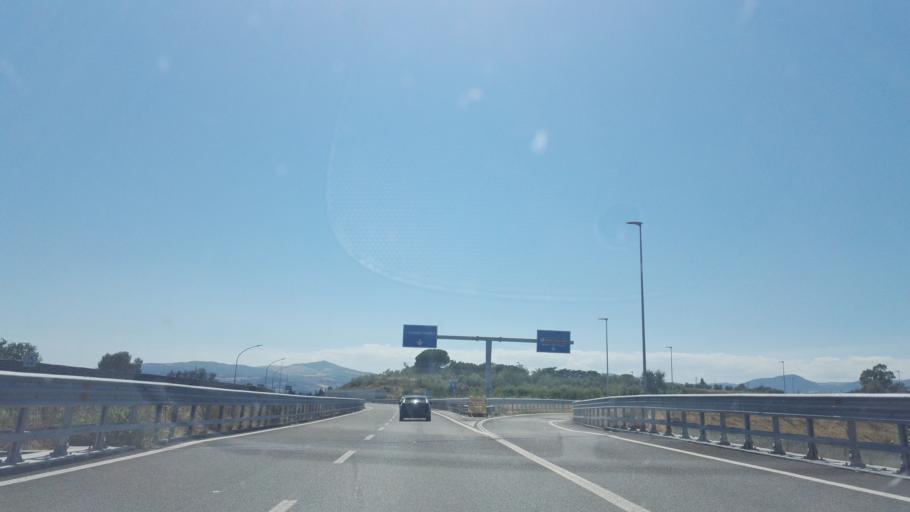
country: IT
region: Basilicate
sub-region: Provincia di Matera
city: Nova Siri Scalo
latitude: 40.1388
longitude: 16.6303
